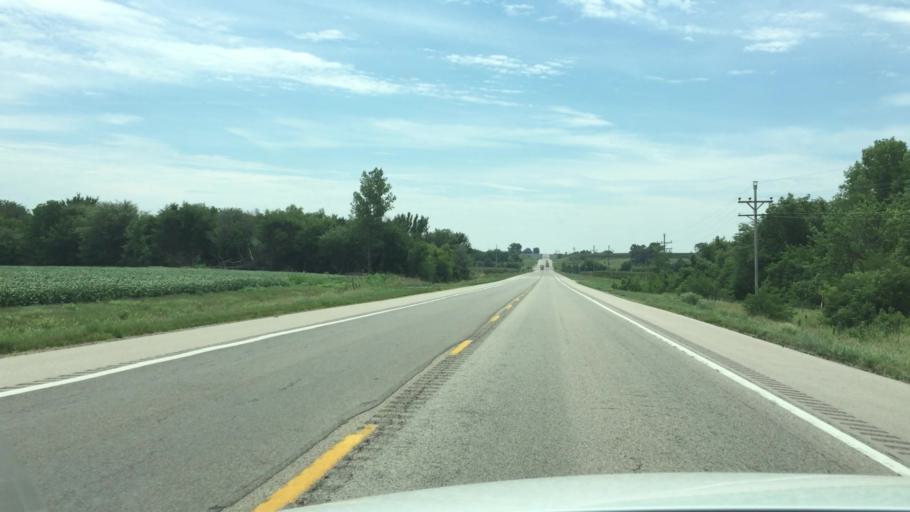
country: US
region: Kansas
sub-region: Nemaha County
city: Sabetha
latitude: 39.8058
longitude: -95.7294
